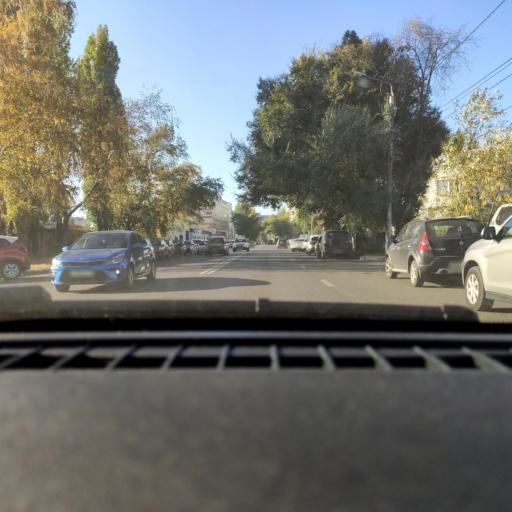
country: RU
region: Voronezj
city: Voronezh
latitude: 51.6779
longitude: 39.2523
